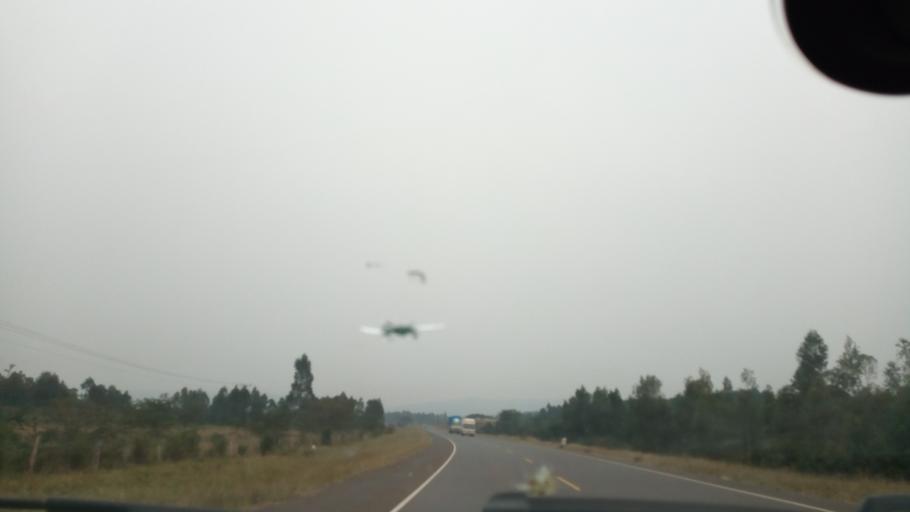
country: UG
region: Western Region
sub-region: Mbarara District
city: Mbarara
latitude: -0.7237
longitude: 30.7288
